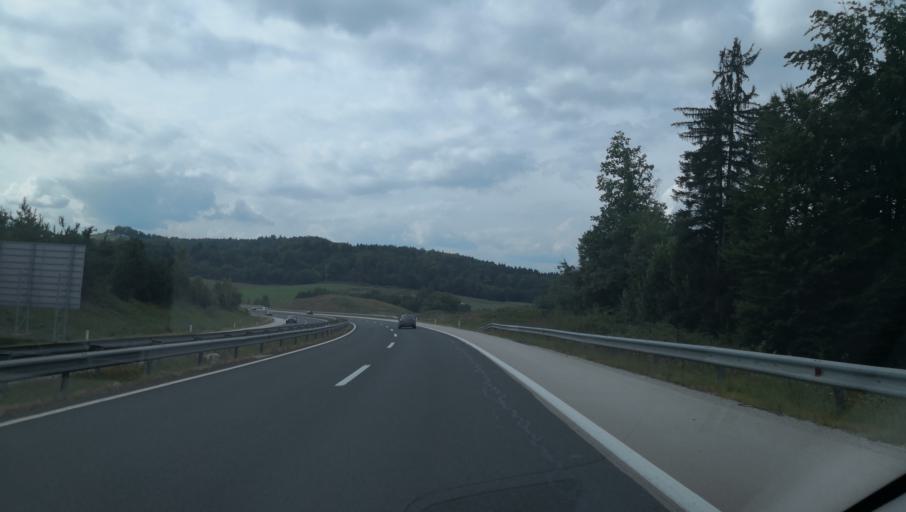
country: SI
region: Trebnje
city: Trebnje
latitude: 45.9171
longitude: 14.9547
